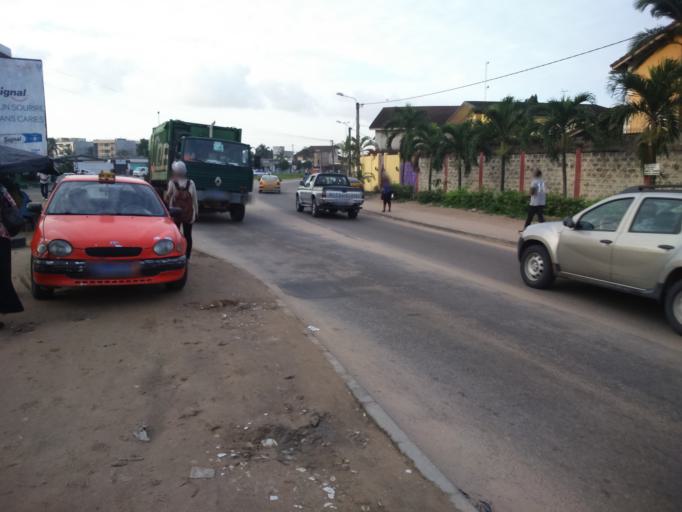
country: CI
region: Lagunes
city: Abobo
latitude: 5.4069
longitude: -3.9910
